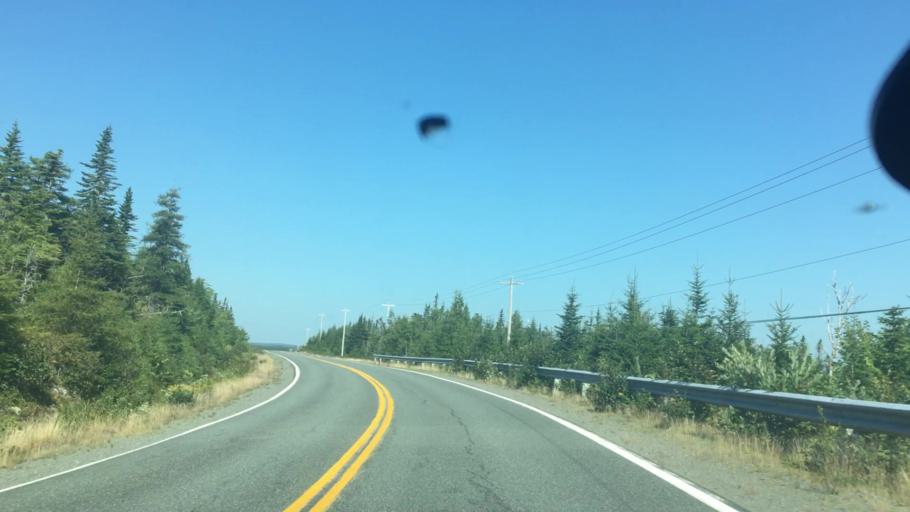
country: CA
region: Nova Scotia
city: Antigonish
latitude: 44.9899
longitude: -62.0957
